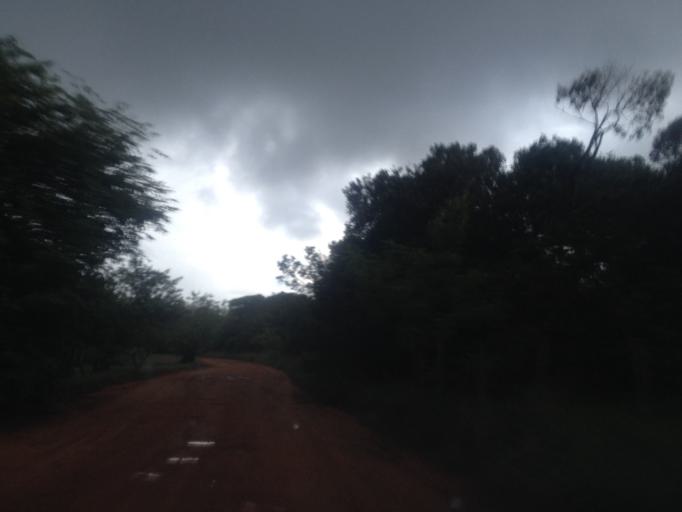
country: BR
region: Bahia
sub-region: Mata De Sao Joao
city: Mata de Sao Joao
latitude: -12.5704
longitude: -38.0224
